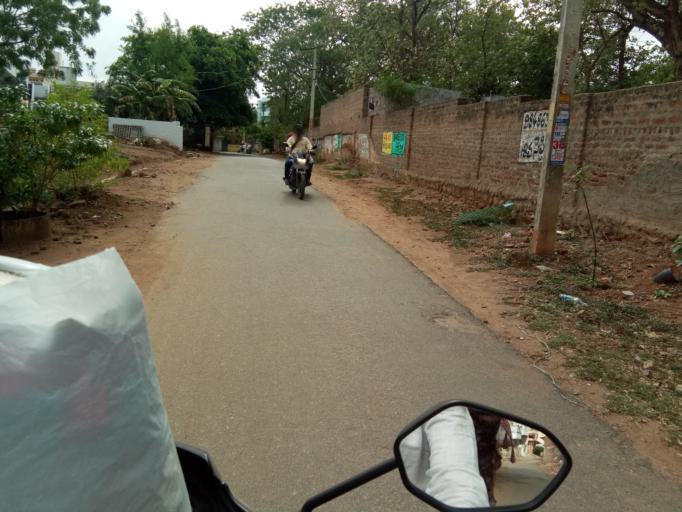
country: IN
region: Telangana
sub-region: Khammam
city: Khammam
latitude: 17.2374
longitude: 80.1466
